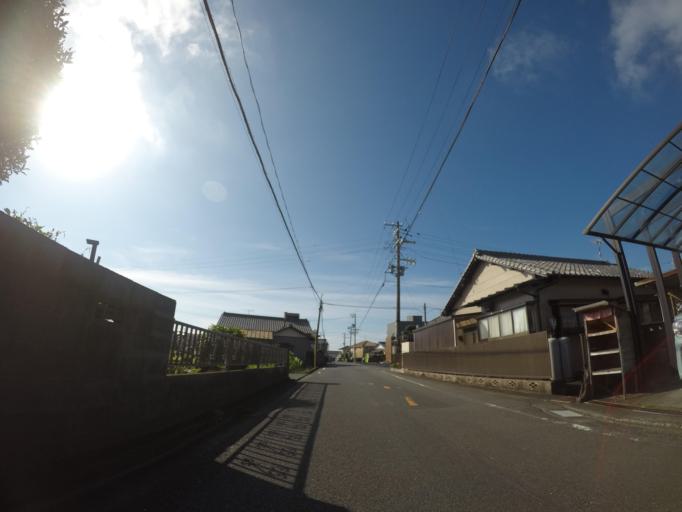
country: JP
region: Shizuoka
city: Fujieda
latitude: 34.7853
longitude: 138.2836
